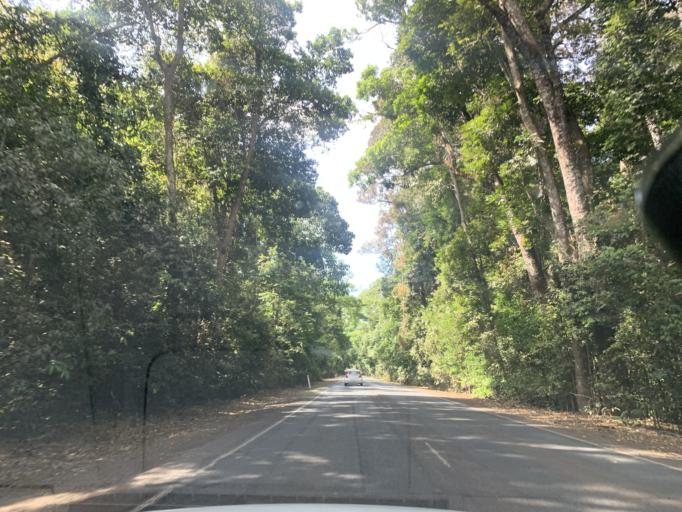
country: AU
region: Queensland
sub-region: Tablelands
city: Tolga
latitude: -17.2386
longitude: 145.4795
